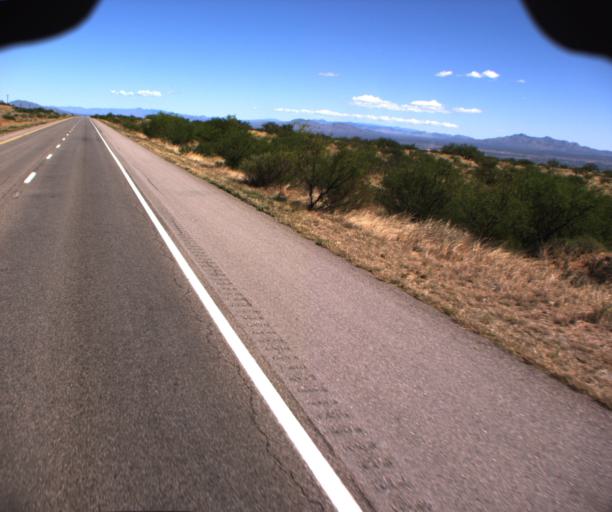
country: US
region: Arizona
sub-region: Cochise County
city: Whetstone
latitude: 31.8726
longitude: -110.3410
